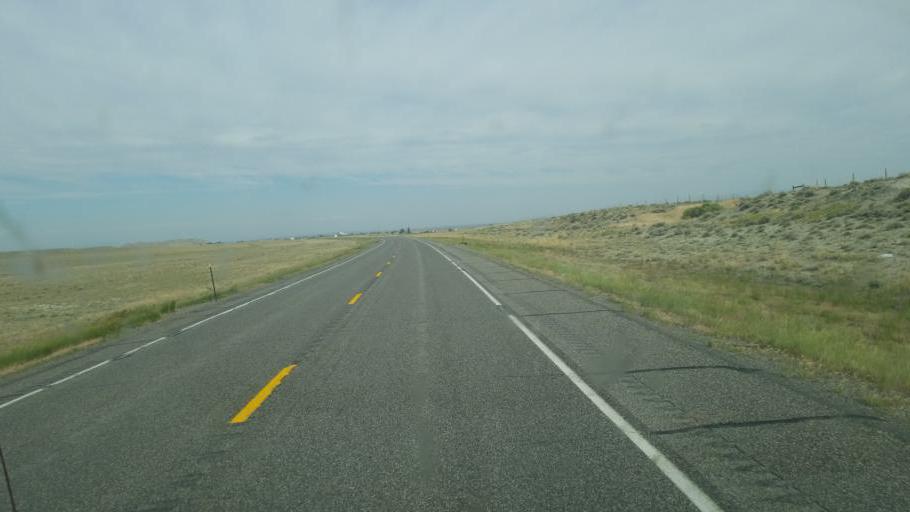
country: US
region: Wyoming
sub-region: Fremont County
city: Riverton
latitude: 43.2360
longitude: -108.0764
